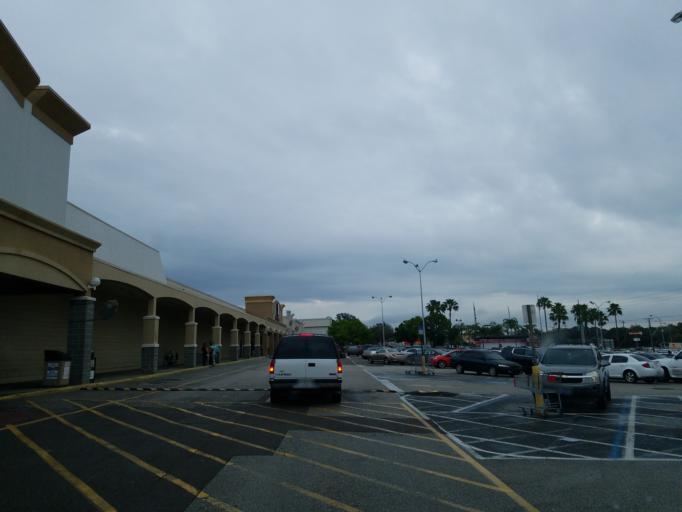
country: US
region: Florida
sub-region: Hillsborough County
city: Brandon
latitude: 27.9388
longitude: -82.3090
